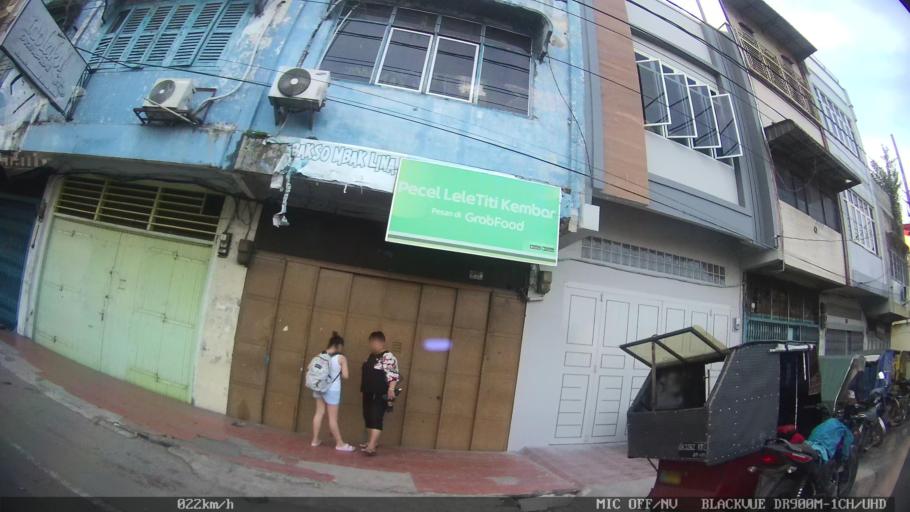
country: ID
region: North Sumatra
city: Binjai
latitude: 3.6108
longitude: 98.4912
